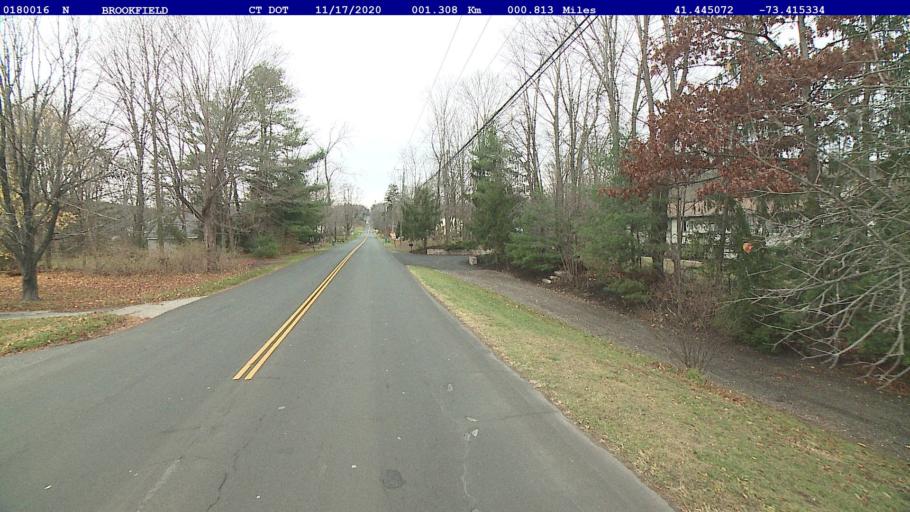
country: US
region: Connecticut
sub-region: Fairfield County
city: Danbury
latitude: 41.4451
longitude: -73.4153
